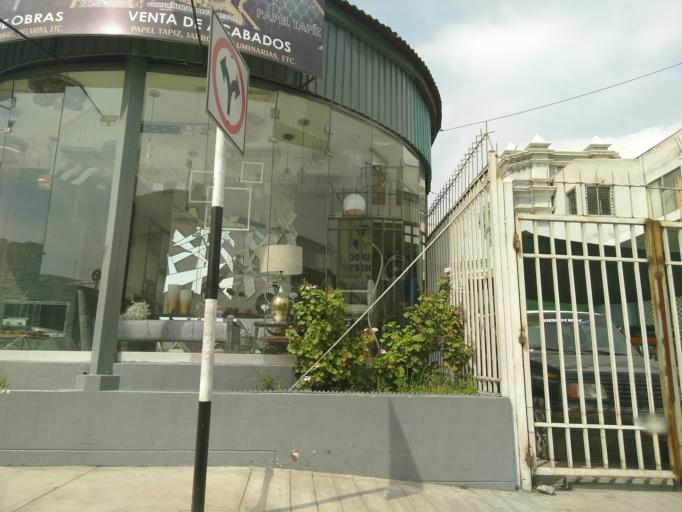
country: PE
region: Arequipa
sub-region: Provincia de Arequipa
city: Arequipa
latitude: -16.4080
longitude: -71.5404
